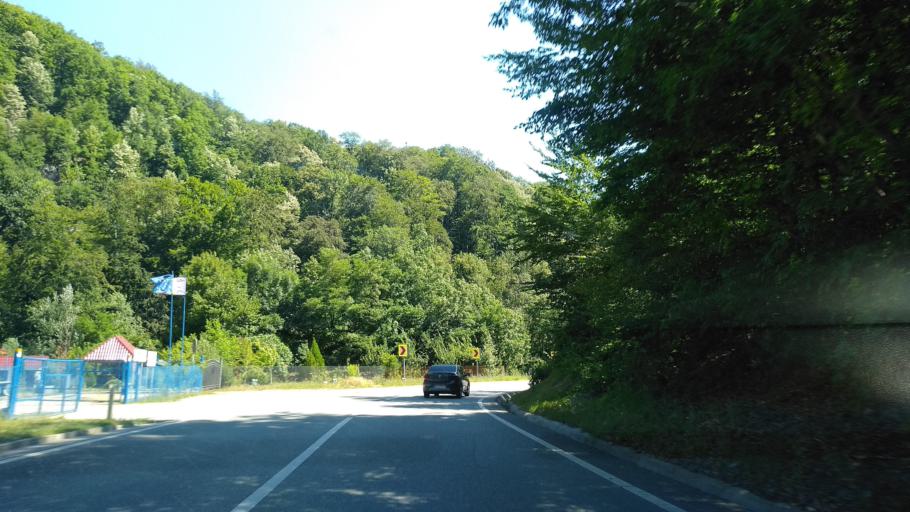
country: RO
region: Gorj
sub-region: Comuna Bumbesti-Jiu
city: Bumbesti-Jiu
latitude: 45.2268
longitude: 23.3833
